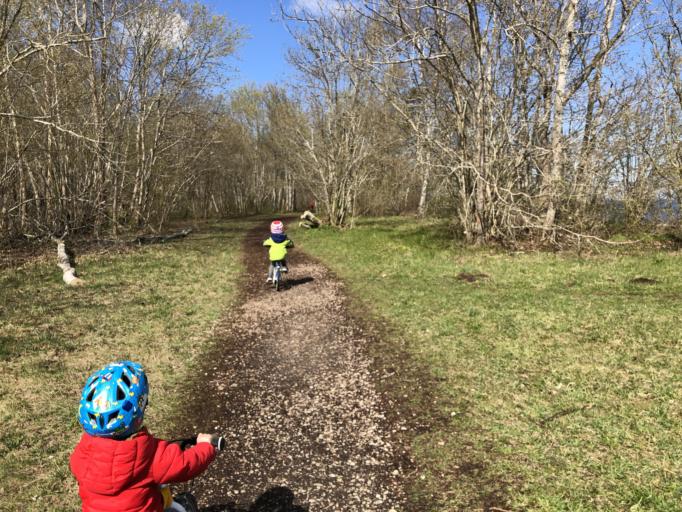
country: EE
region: Harju
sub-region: Harku vald
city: Tabasalu
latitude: 59.4394
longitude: 24.5348
